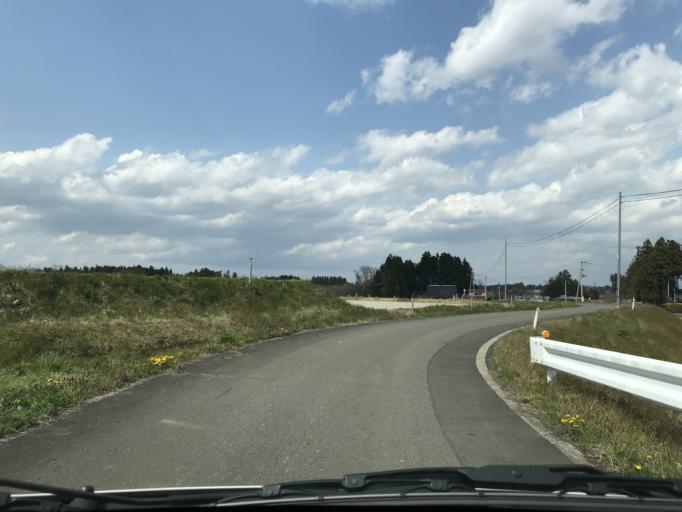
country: JP
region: Iwate
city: Mizusawa
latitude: 39.0695
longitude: 141.1050
